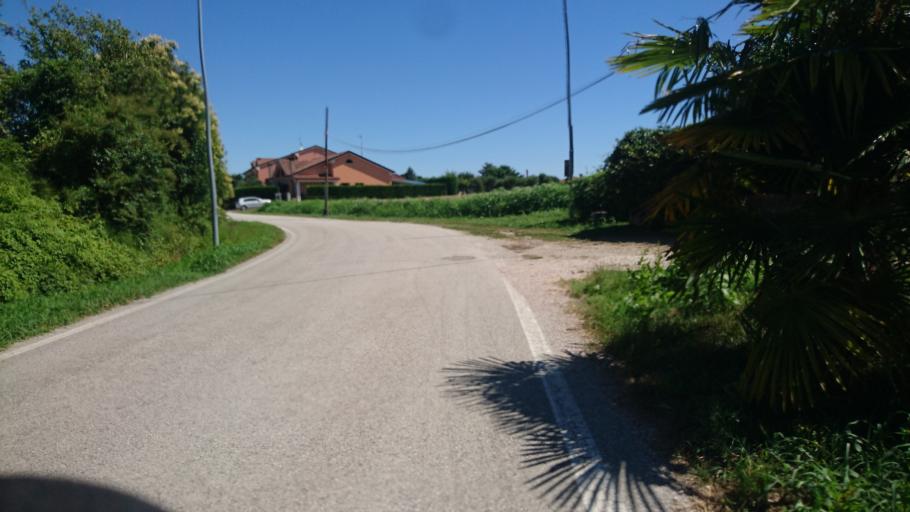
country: IT
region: Veneto
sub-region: Provincia di Padova
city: Campagnola
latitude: 45.2738
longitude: 12.0080
